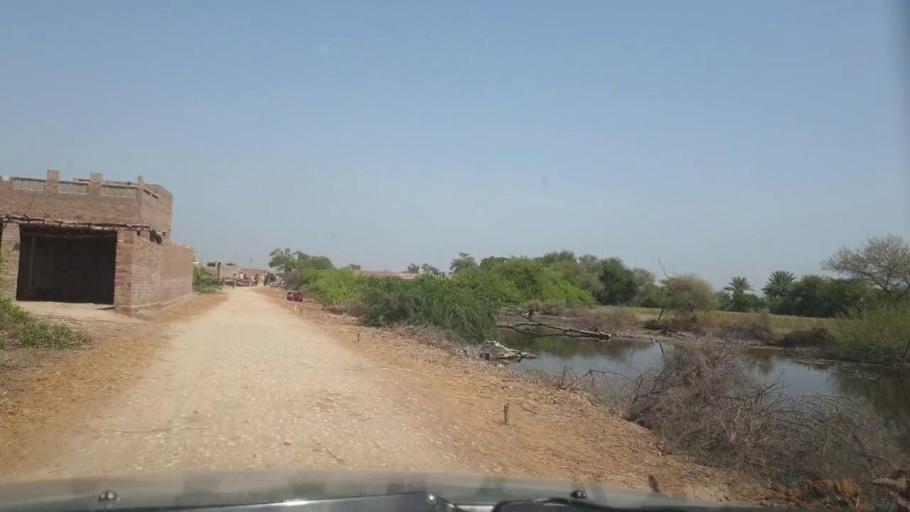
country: PK
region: Sindh
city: Tando Ghulam Ali
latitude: 25.1478
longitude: 68.7654
